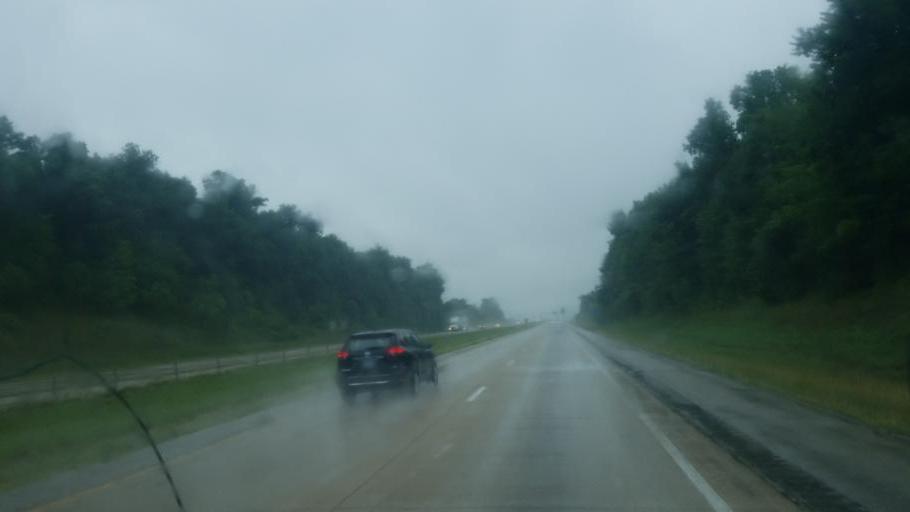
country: US
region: Indiana
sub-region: Grant County
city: Upland
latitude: 40.4899
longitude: -85.5493
